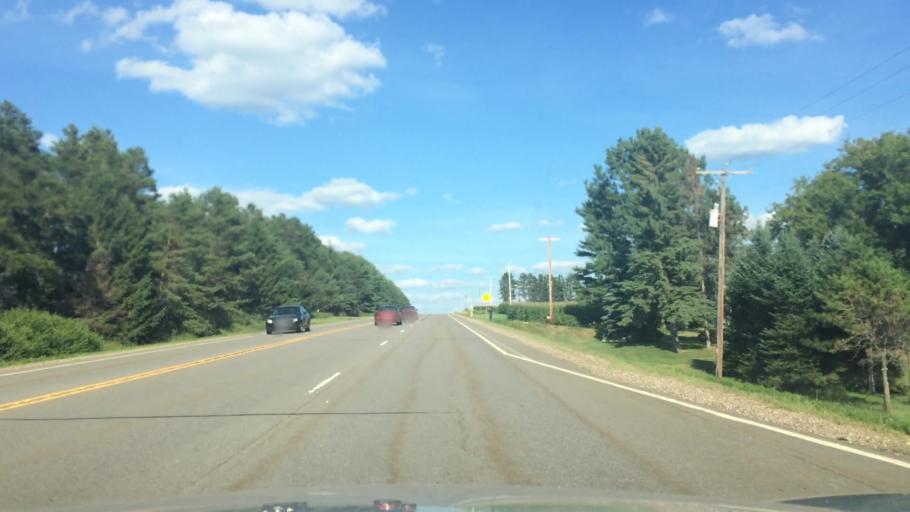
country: US
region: Wisconsin
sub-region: Lincoln County
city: Merrill
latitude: 45.1780
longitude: -89.6183
